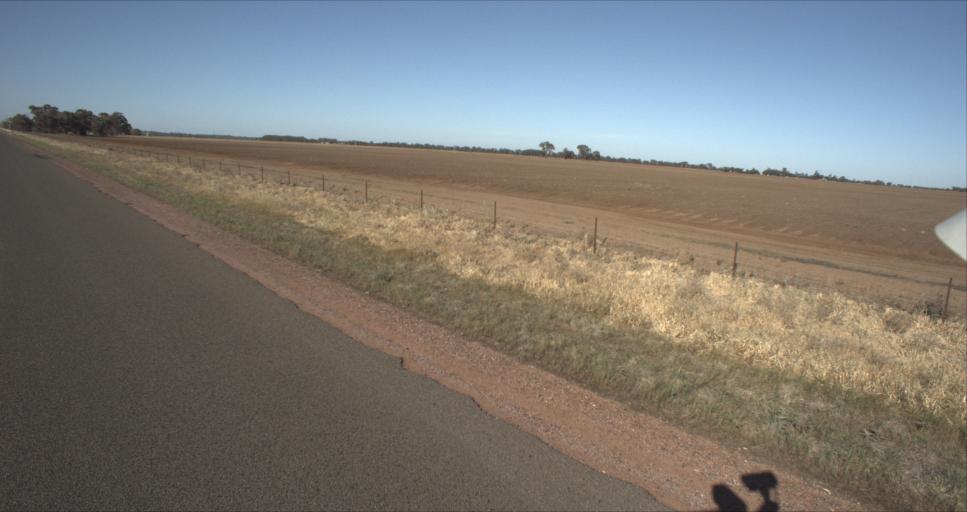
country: AU
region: New South Wales
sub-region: Leeton
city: Leeton
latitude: -34.5726
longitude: 146.2632
